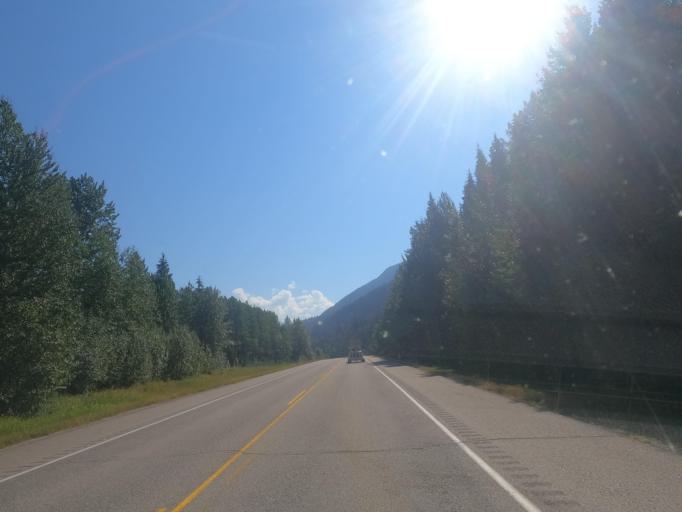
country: CA
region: Alberta
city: Jasper Park Lodge
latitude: 52.8587
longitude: -118.1701
